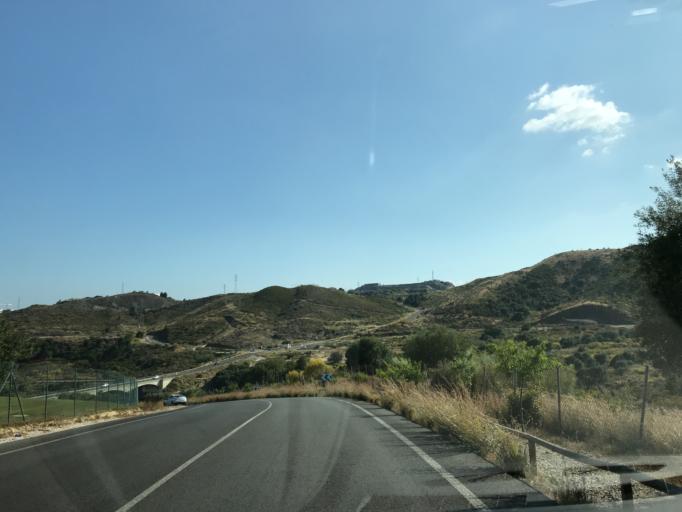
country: ES
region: Andalusia
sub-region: Provincia de Malaga
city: Benahavis
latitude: 36.5049
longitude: -5.0241
